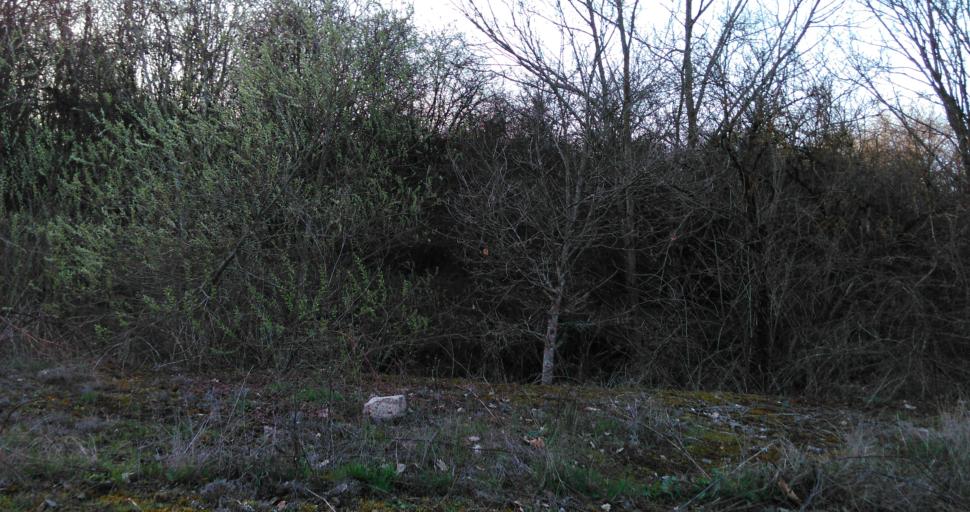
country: FR
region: Lorraine
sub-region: Departement de Meurthe-et-Moselle
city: Saulnes
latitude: 49.5467
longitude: 5.8190
